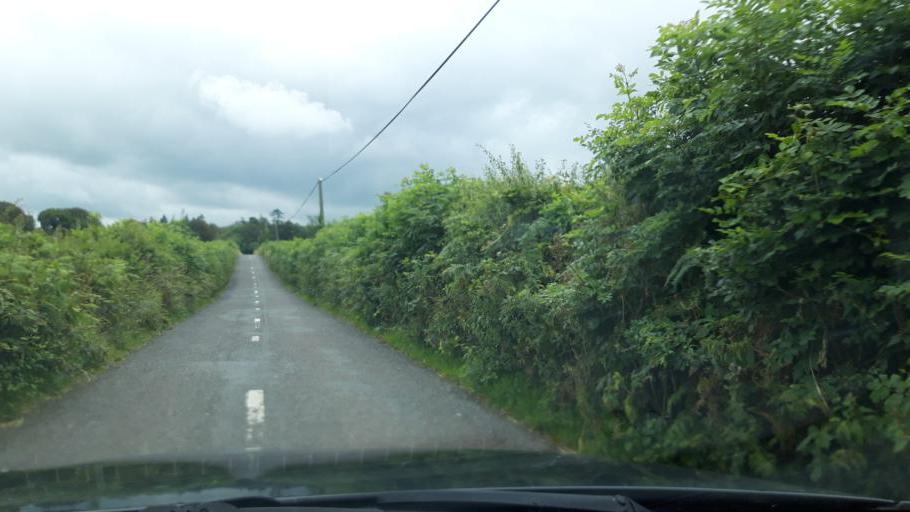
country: IE
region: Munster
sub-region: County Cork
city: Castlemartyr
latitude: 52.1335
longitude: -8.0100
